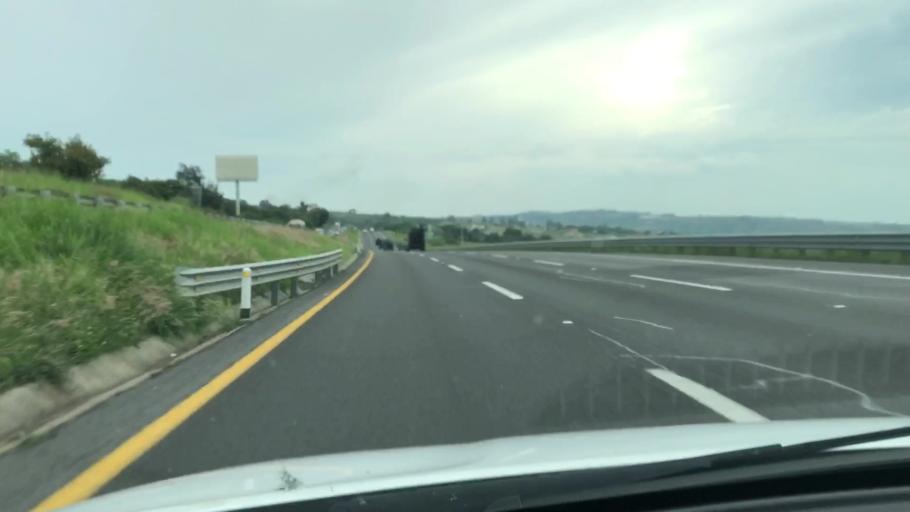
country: MX
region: Jalisco
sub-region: Tonala
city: Mismaloya (Fraccionamiento Pedregal de Santa Martha)
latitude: 20.6109
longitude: -103.1734
